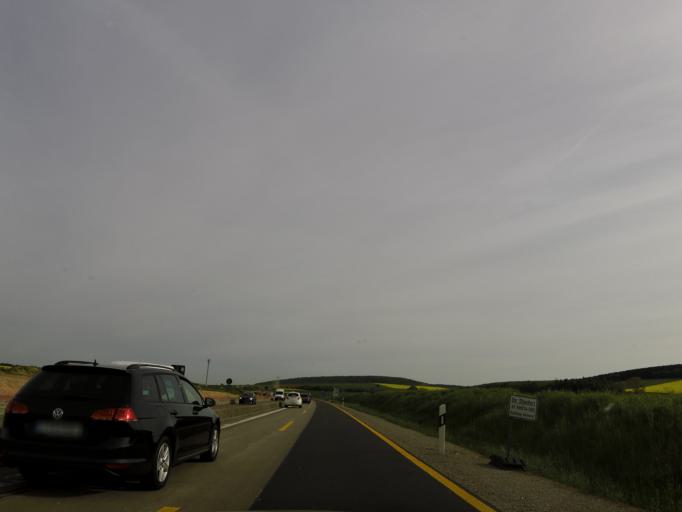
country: DE
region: Lower Saxony
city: Seesen
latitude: 51.9338
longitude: 10.1454
